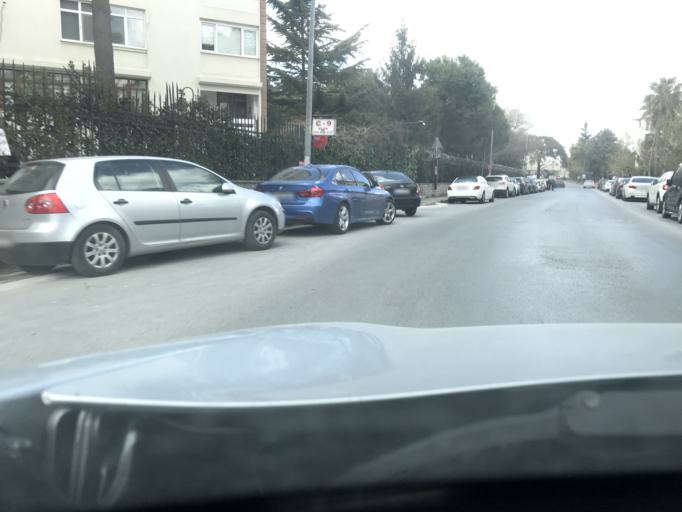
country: TR
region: Istanbul
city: Bahcelievler
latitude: 40.9612
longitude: 28.8174
